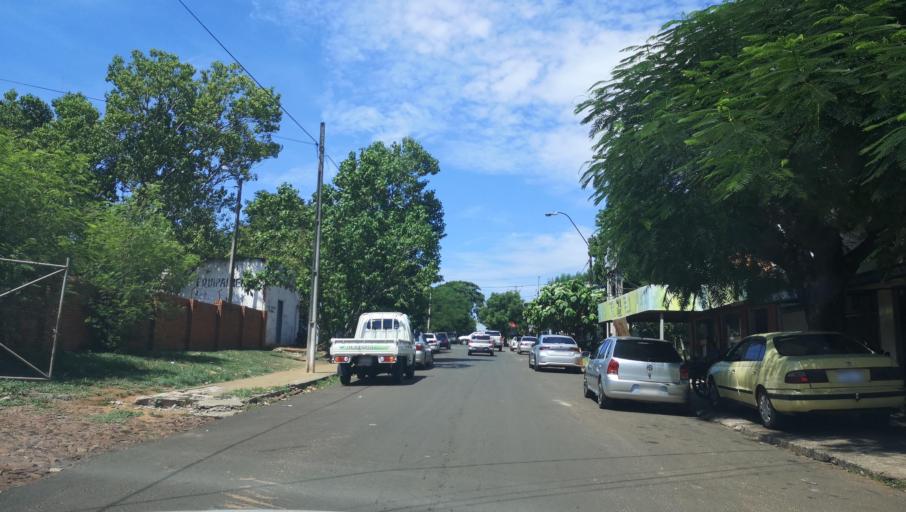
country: PY
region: Misiones
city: Santa Maria
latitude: -26.8860
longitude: -57.0272
